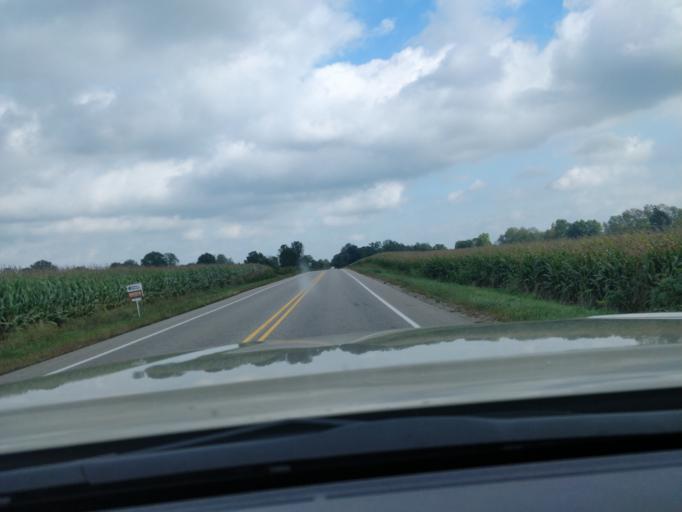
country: US
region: Michigan
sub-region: Kent County
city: Lowell
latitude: 42.8859
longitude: -85.3311
